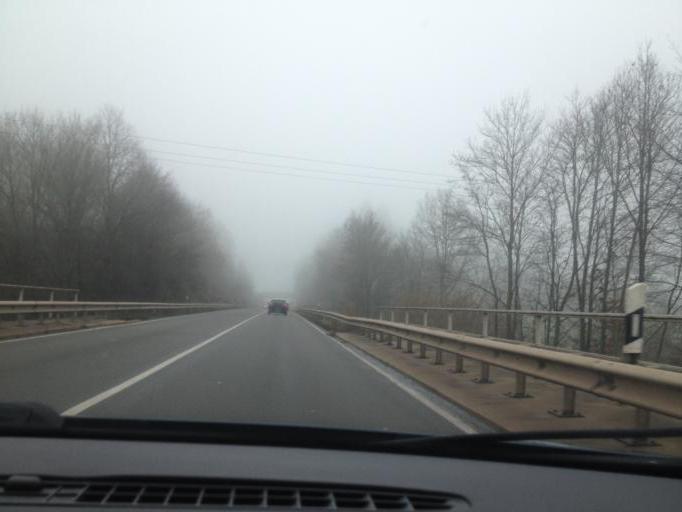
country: DE
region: Rheinland-Pfalz
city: Katzweiler
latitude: 49.4754
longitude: 7.6965
